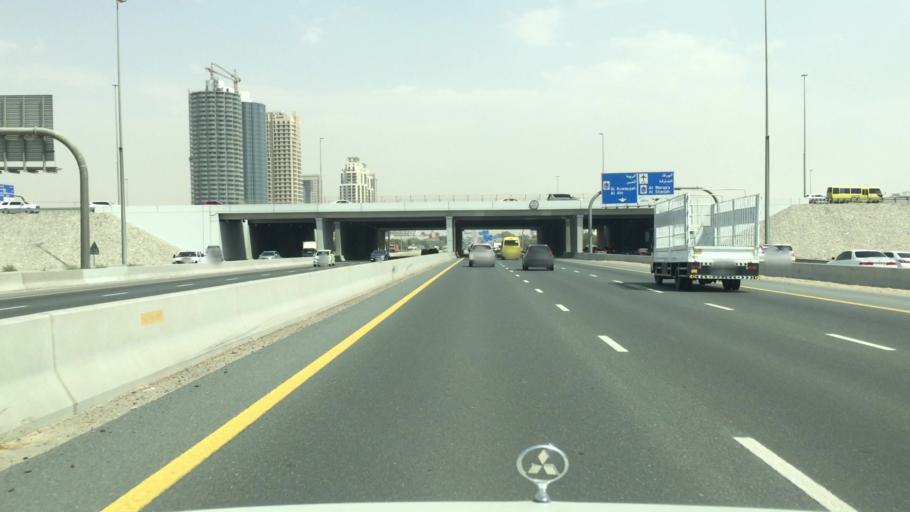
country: AE
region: Dubai
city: Dubai
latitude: 25.1208
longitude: 55.3641
